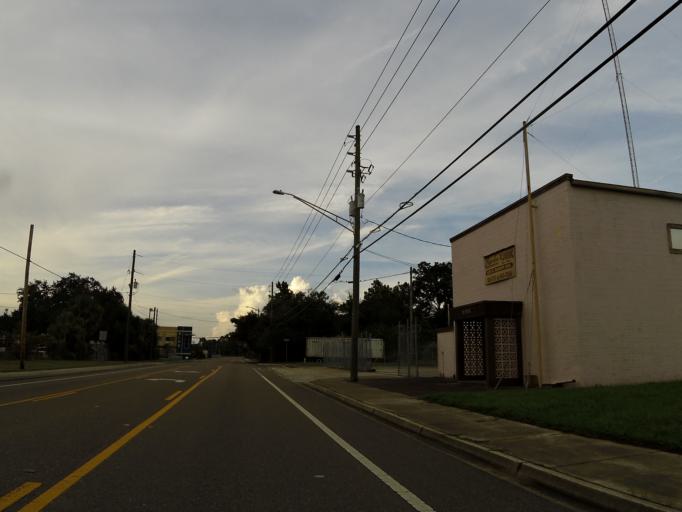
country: US
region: Florida
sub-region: Duval County
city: Jacksonville
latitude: 30.3392
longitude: -81.7055
